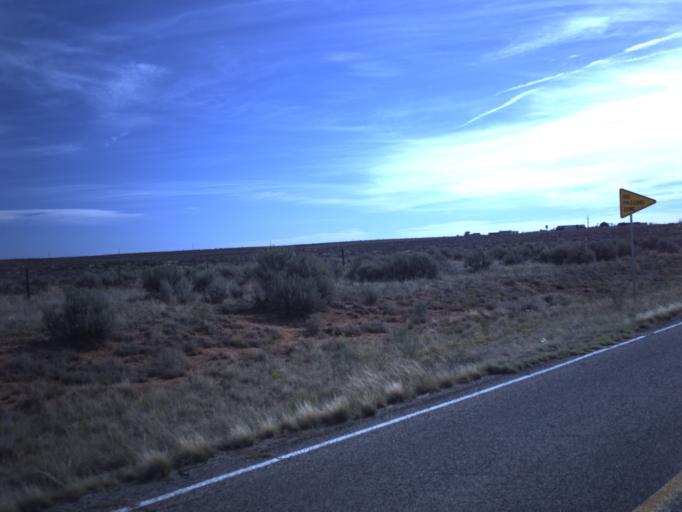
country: US
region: Utah
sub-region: San Juan County
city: Blanding
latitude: 37.4242
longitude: -109.3443
